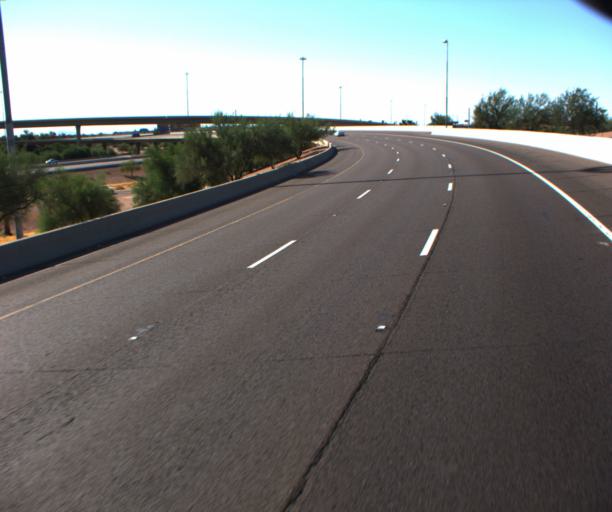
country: US
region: Arizona
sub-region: Maricopa County
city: Guadalupe
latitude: 33.3904
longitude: -111.9694
